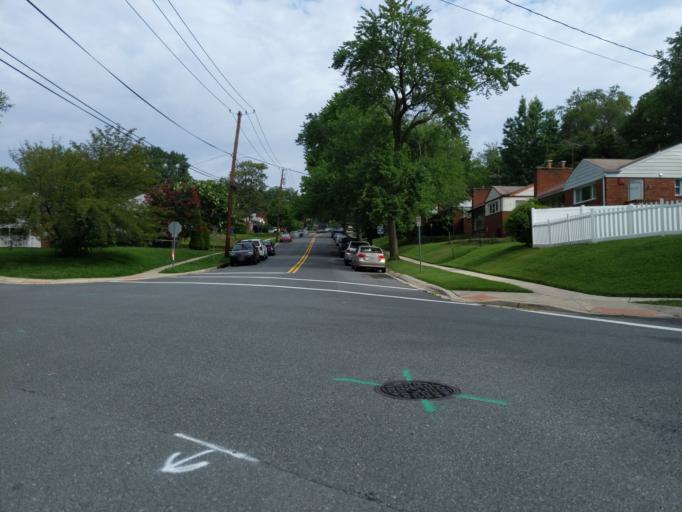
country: US
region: Maryland
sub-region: Montgomery County
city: Forest Glen
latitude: 39.0245
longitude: -77.0547
